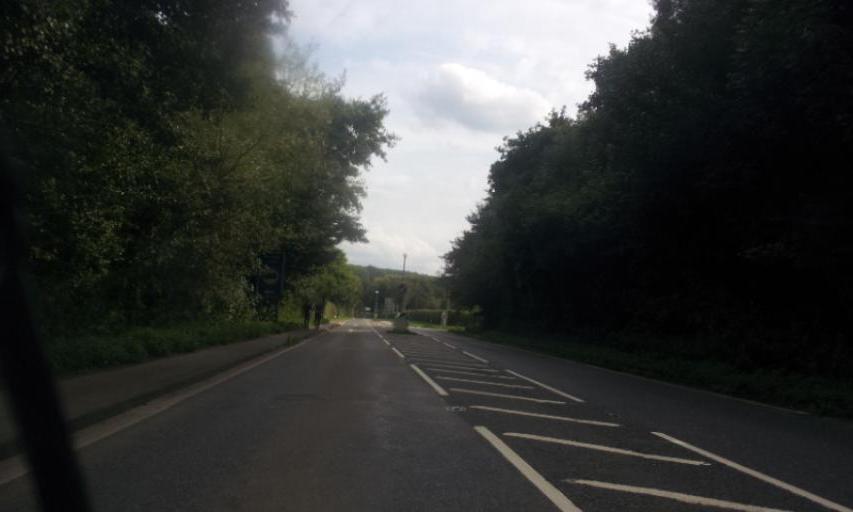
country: GB
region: England
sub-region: Kent
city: Kings Hill
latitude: 51.2571
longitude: 0.3687
